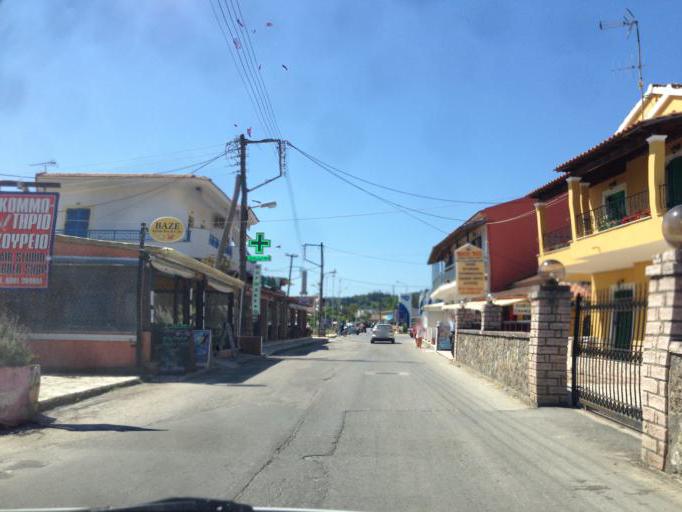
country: GR
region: Ionian Islands
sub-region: Nomos Kerkyras
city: Agios Georgis
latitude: 39.7840
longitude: 19.7081
